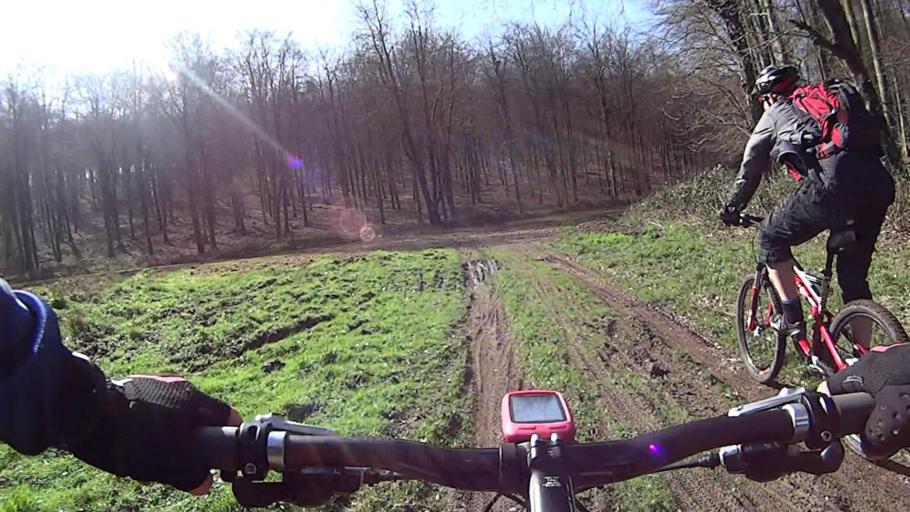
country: GB
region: England
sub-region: West Sussex
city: Midhurst
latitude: 50.9272
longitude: -0.7198
